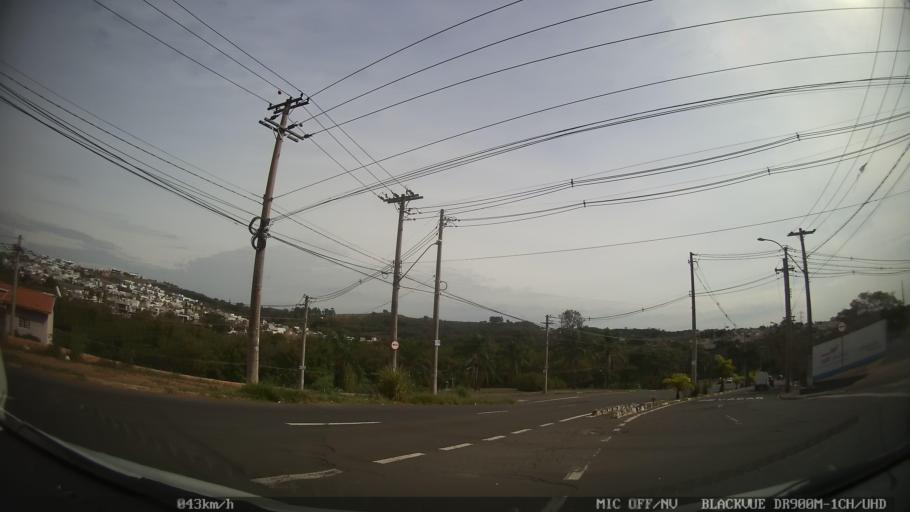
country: BR
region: Sao Paulo
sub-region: Piracicaba
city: Piracicaba
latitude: -22.7325
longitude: -47.6706
